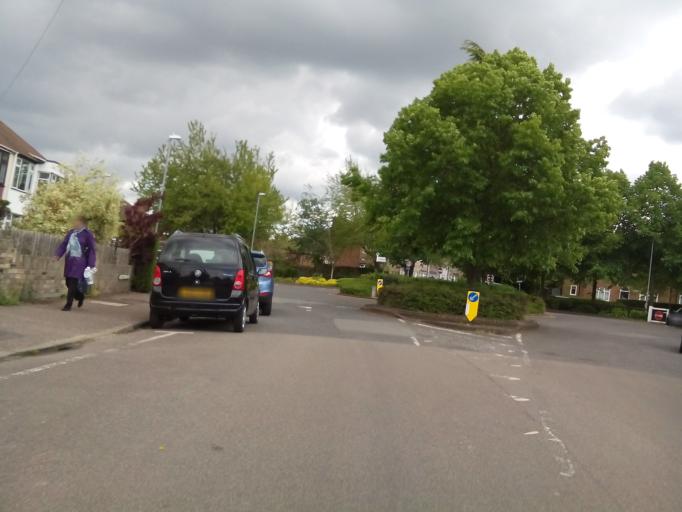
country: GB
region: England
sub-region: Cambridgeshire
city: Cambridge
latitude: 52.2024
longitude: 0.1468
